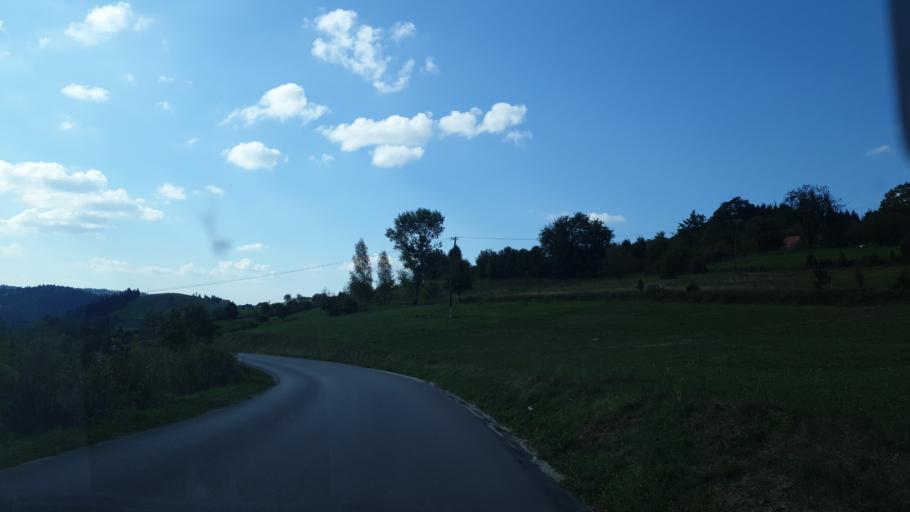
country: RS
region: Central Serbia
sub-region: Zlatiborski Okrug
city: Nova Varos
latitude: 43.4369
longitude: 19.8702
